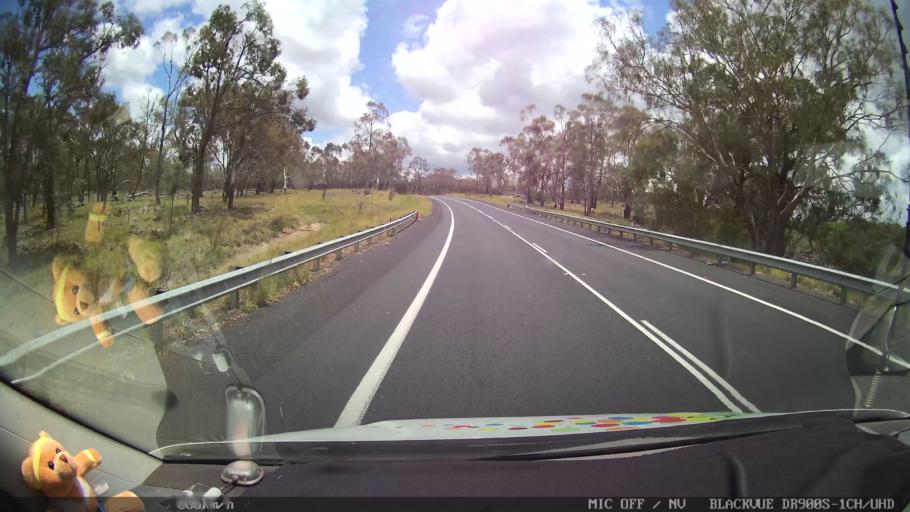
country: AU
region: New South Wales
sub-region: Glen Innes Severn
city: Glen Innes
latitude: -29.3671
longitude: 151.8983
